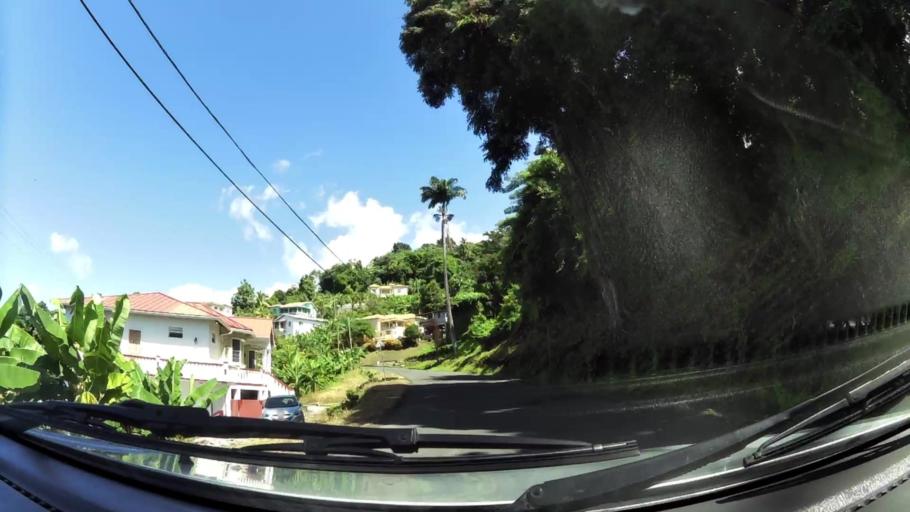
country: GD
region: Saint John
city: Gouyave
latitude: 12.1131
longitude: -61.7468
